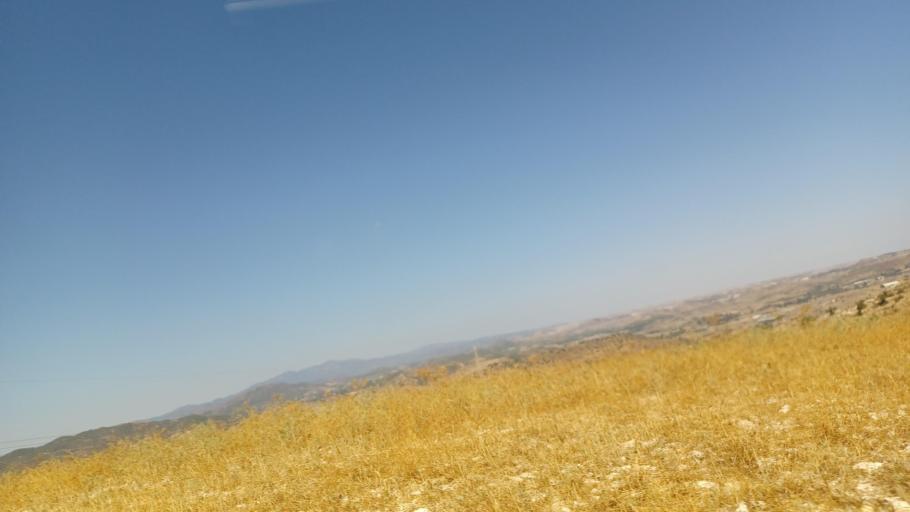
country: CY
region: Larnaka
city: Psevdas
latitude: 34.9594
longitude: 33.4826
